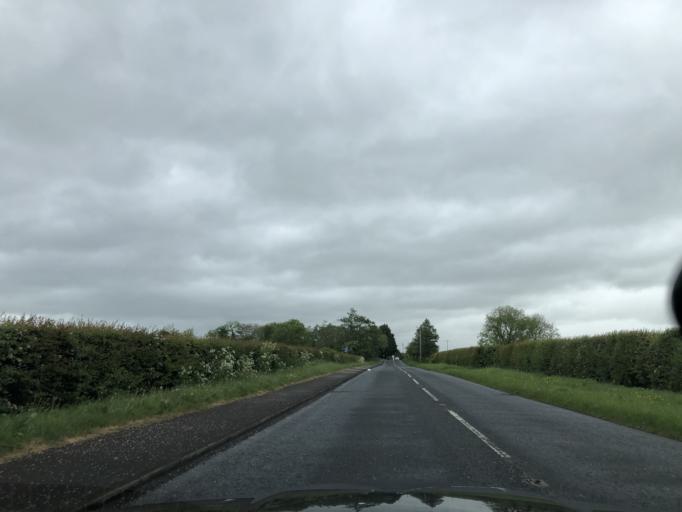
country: GB
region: Northern Ireland
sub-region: Ballymoney District
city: Ballymoney
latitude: 55.0821
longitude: -6.5119
